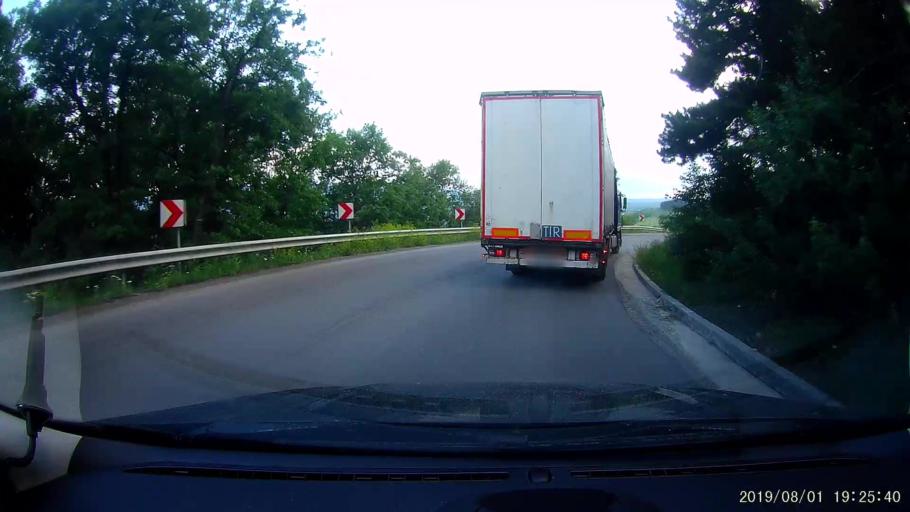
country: BG
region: Burgas
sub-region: Obshtina Sungurlare
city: Sungurlare
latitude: 42.8589
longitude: 26.9462
